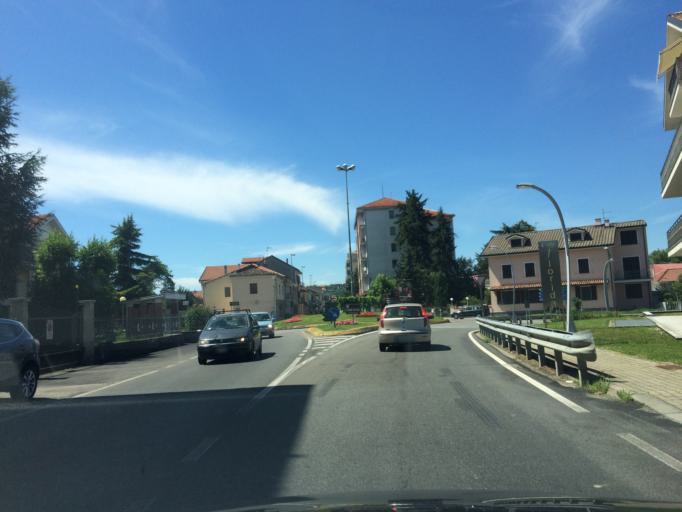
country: IT
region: Piedmont
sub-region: Provincia di Asti
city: Nizza Monferrato
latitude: 44.7693
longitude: 8.3657
